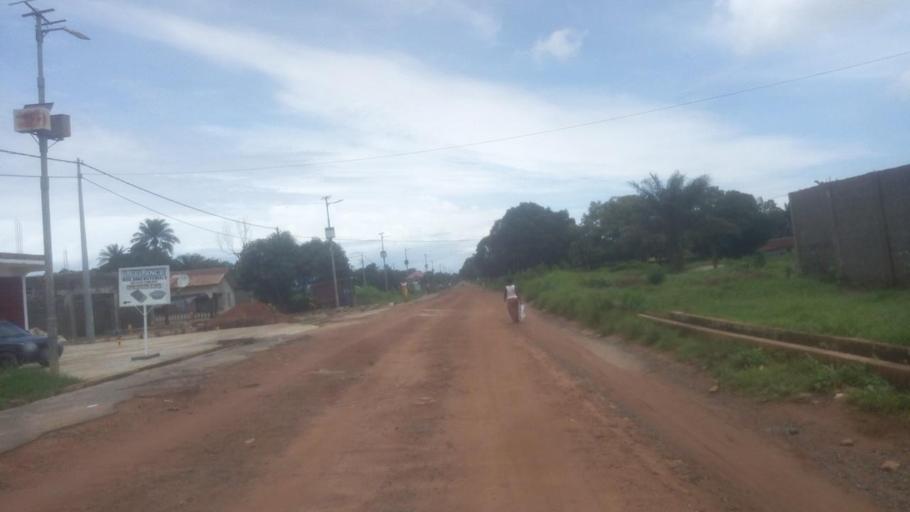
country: SL
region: Northern Province
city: Masoyila
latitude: 8.6019
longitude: -13.1892
